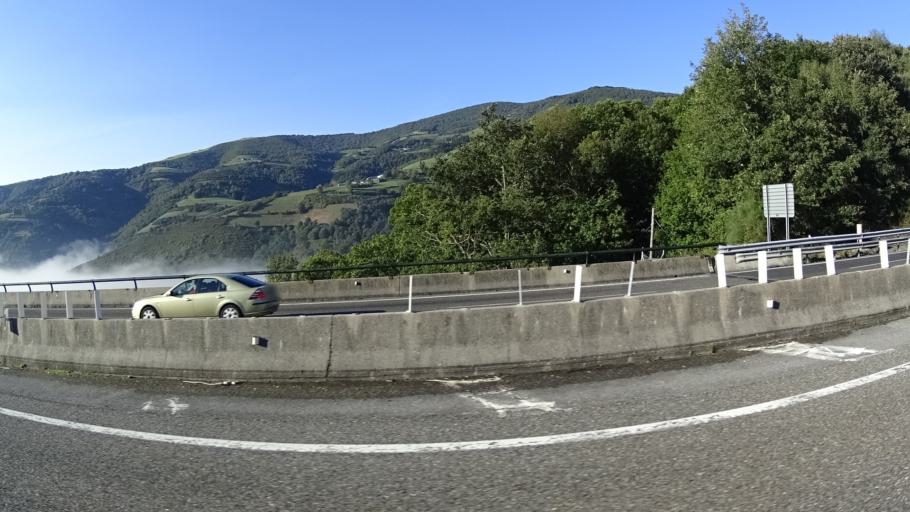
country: ES
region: Galicia
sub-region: Provincia de Lugo
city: San Roman
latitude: 42.7627
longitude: -7.0794
